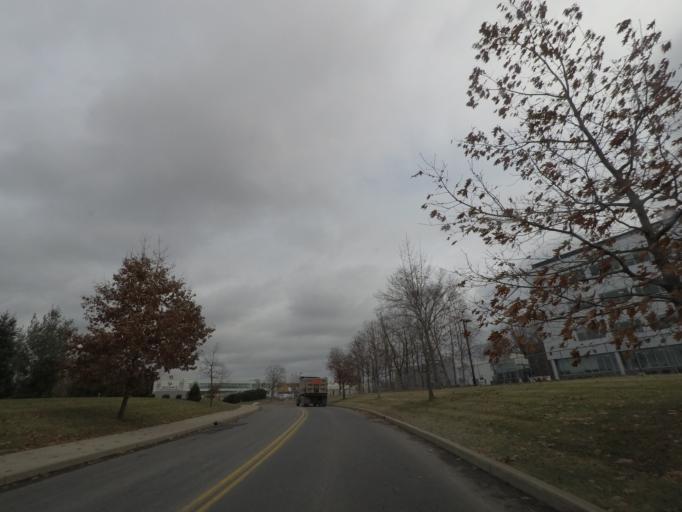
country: US
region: New York
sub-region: Rensselaer County
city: Hampton Manor
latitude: 42.6271
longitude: -73.7354
